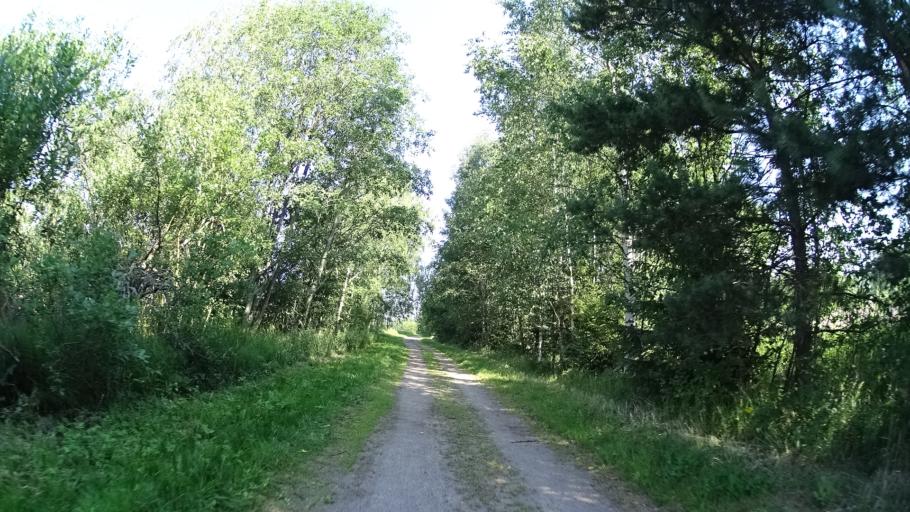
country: FI
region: Uusimaa
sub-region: Helsinki
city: Kerava
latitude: 60.3535
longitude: 25.1260
